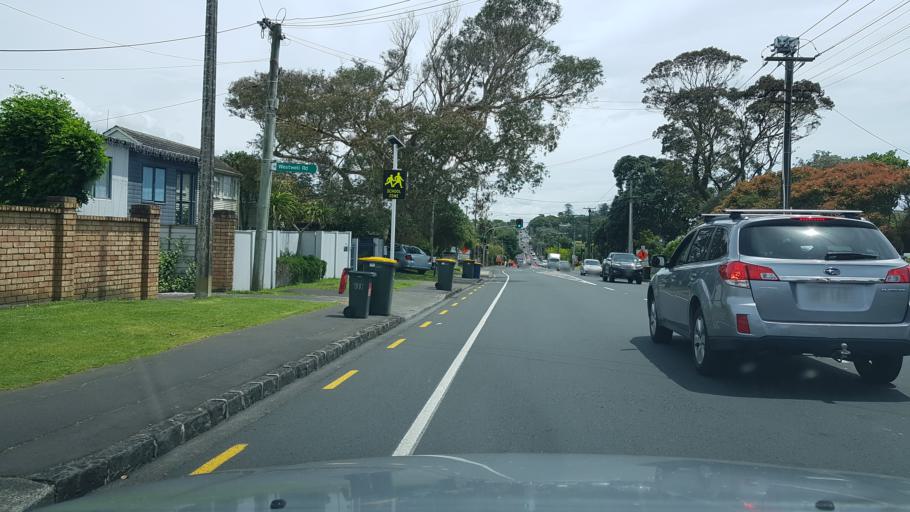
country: NZ
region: Auckland
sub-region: Auckland
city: North Shore
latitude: -36.8061
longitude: 174.7891
